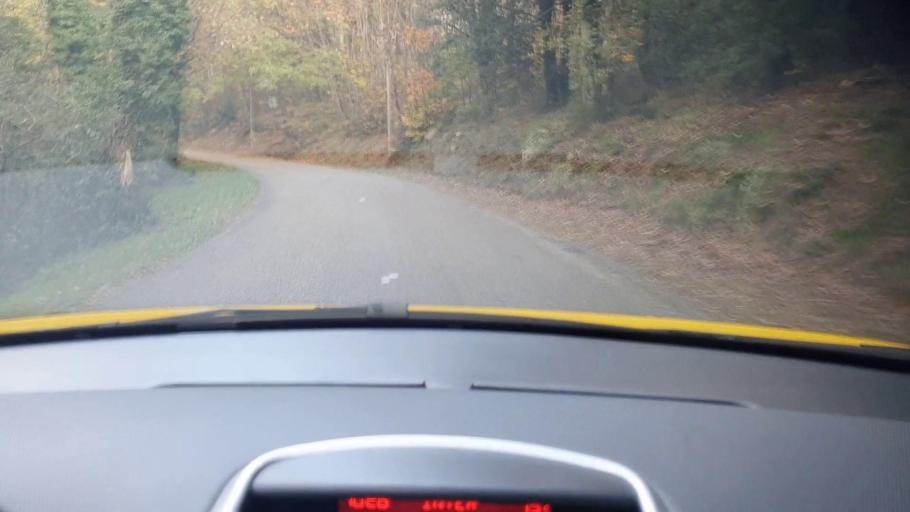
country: FR
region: Languedoc-Roussillon
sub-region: Departement du Gard
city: Lasalle
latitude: 44.0275
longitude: 3.8352
